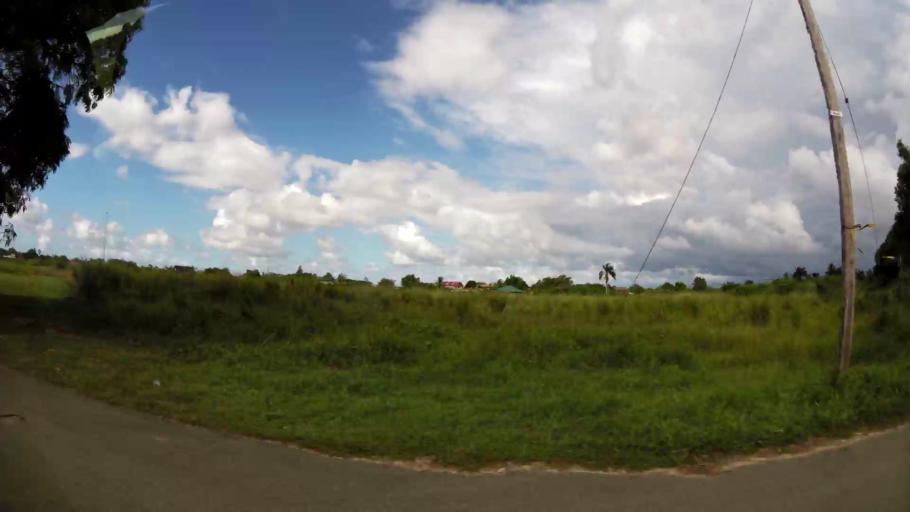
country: SR
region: Paramaribo
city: Paramaribo
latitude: 5.8491
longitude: -55.1579
